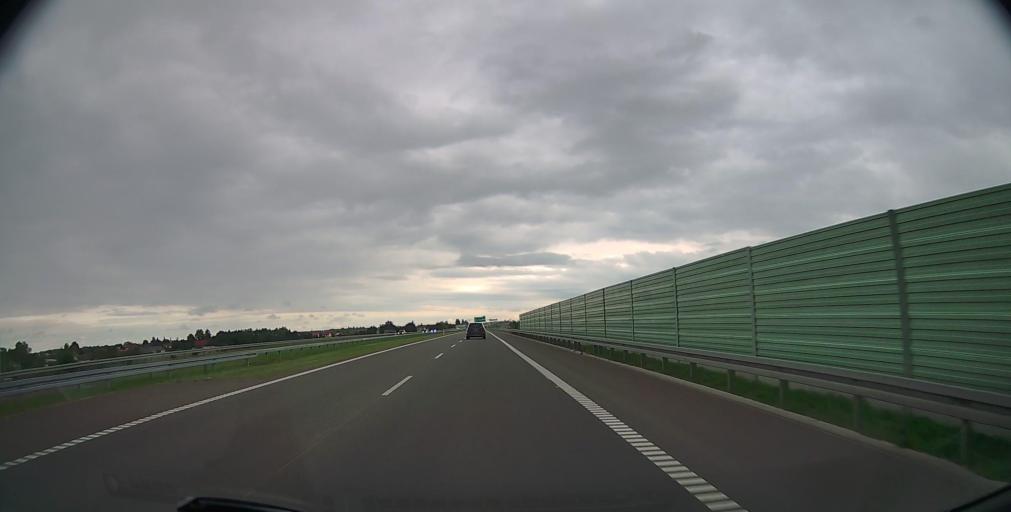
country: PL
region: Masovian Voivodeship
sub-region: Powiat radomski
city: Zakrzew
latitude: 51.4321
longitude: 21.0326
